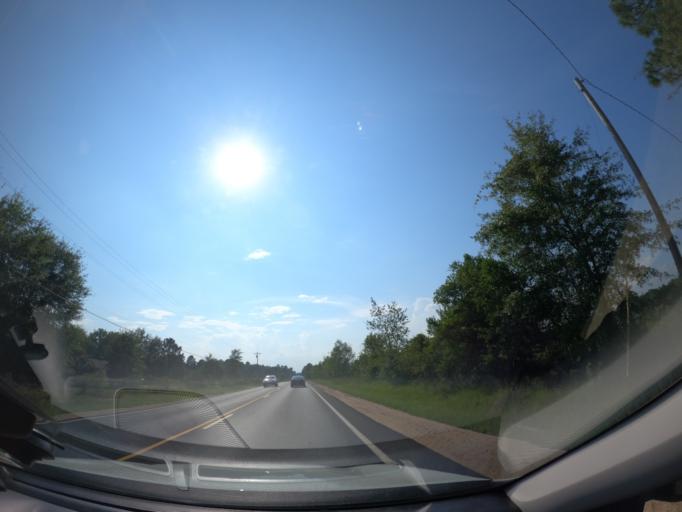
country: US
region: South Carolina
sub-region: Aiken County
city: New Ellenton
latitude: 33.3927
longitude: -81.7247
